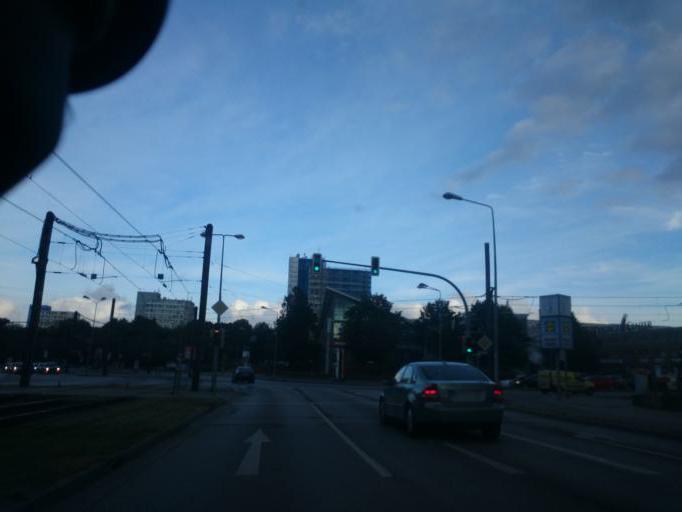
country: DE
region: Mecklenburg-Vorpommern
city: Rostock
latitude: 54.0720
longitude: 12.1155
